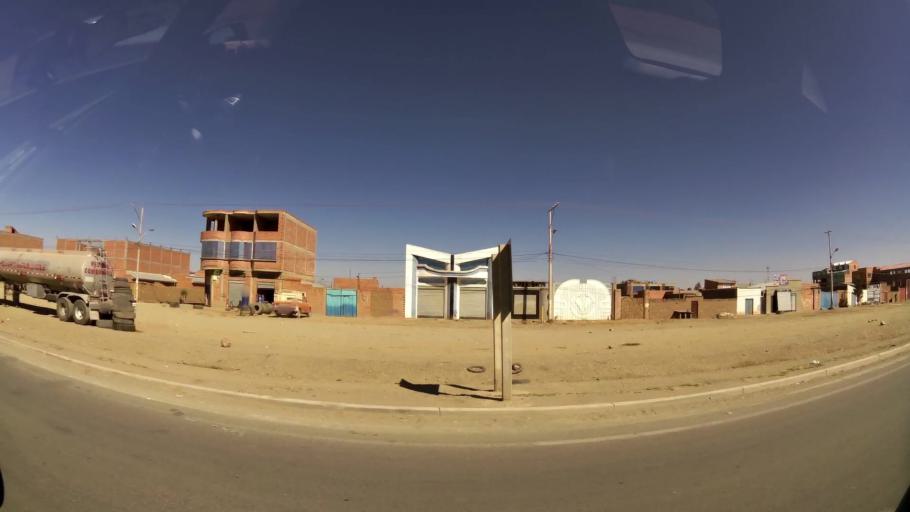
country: BO
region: La Paz
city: La Paz
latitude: -16.6102
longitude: -68.1831
